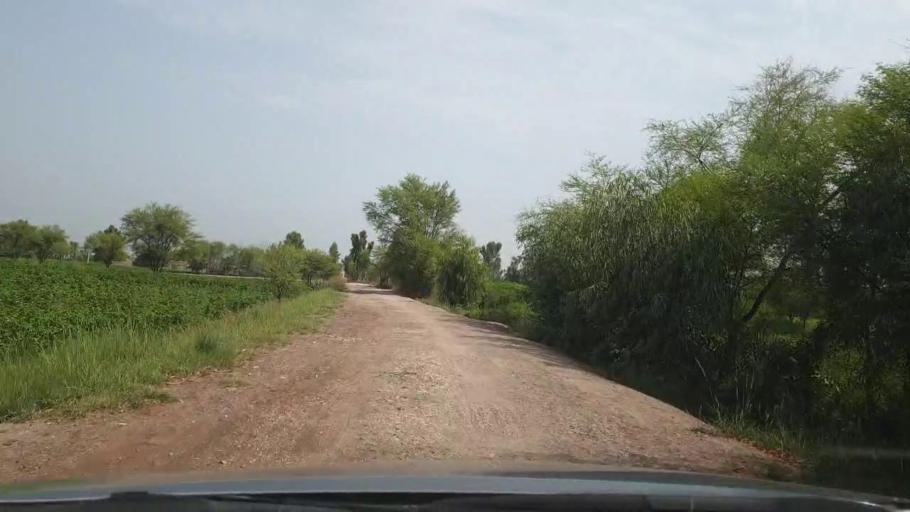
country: PK
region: Sindh
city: Rohri
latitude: 27.6561
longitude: 69.0244
